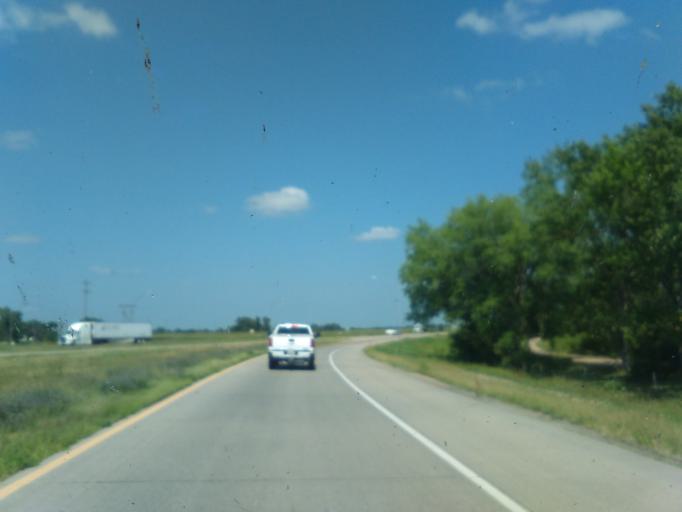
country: US
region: Nebraska
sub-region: Phelps County
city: Holdrege
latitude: 40.6895
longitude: -99.3774
